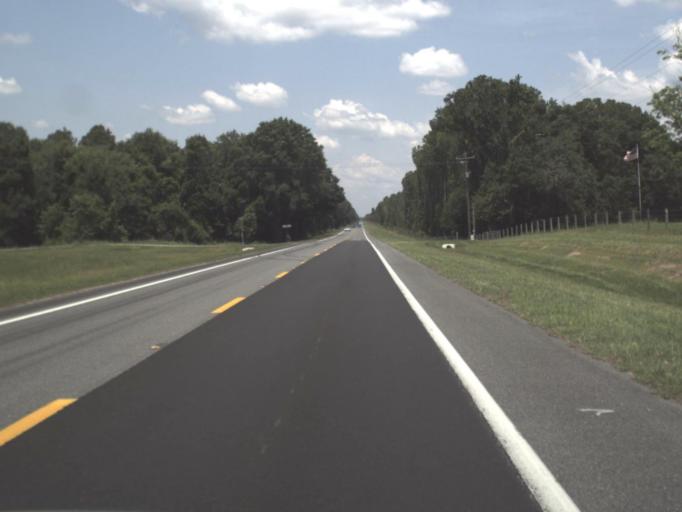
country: US
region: Florida
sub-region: Union County
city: Lake Butler
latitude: 30.0376
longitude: -82.3780
